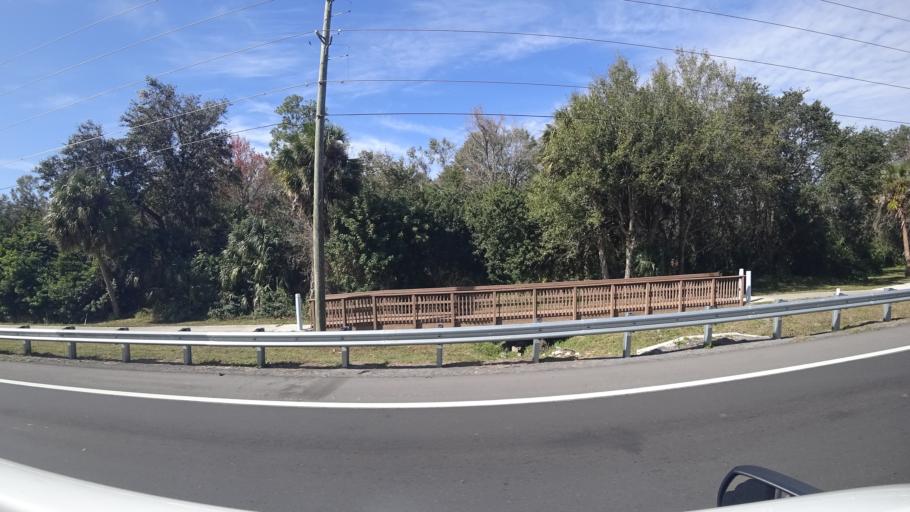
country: US
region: Florida
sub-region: Manatee County
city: Ellenton
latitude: 27.5292
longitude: -82.4282
